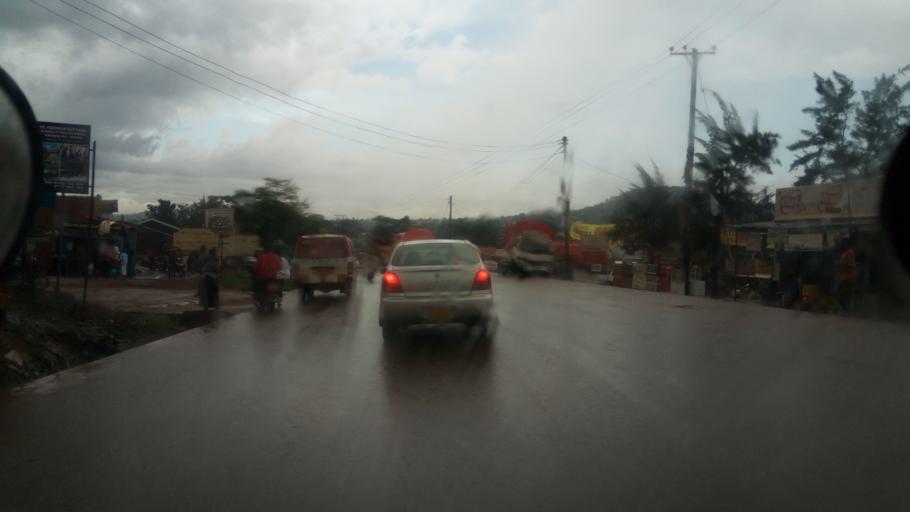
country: UG
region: Central Region
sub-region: Wakiso District
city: Wakiso
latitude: 0.3985
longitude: 32.4792
